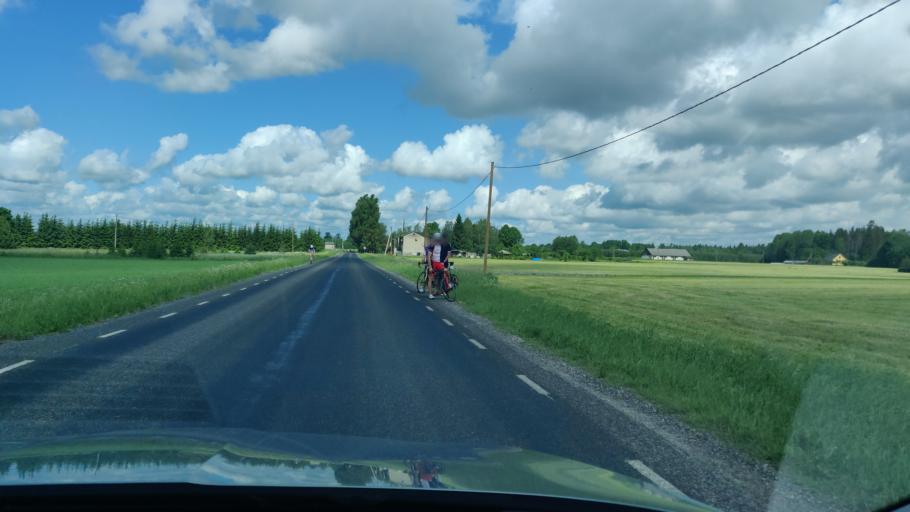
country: EE
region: Jaervamaa
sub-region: Paide linn
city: Paide
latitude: 58.8672
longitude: 25.6037
